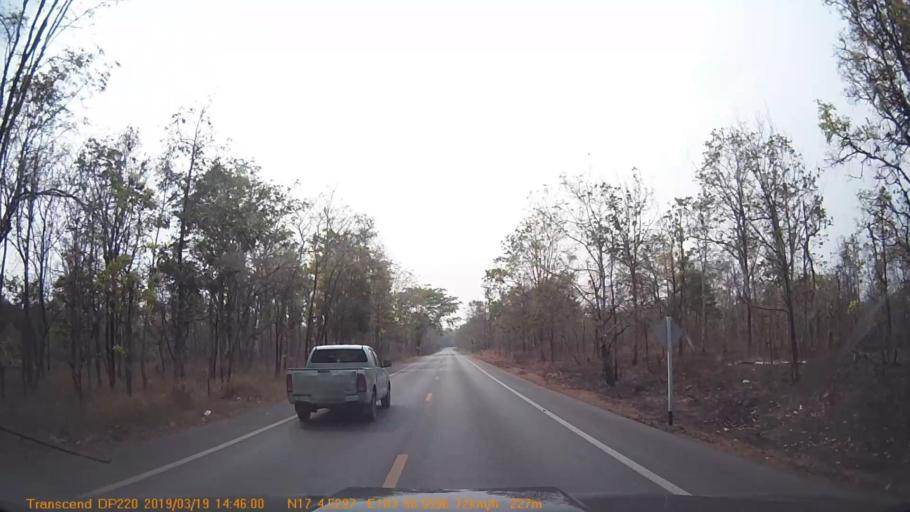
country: TH
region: Sakon Nakhon
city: Phu Phan
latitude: 17.0757
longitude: 103.9423
